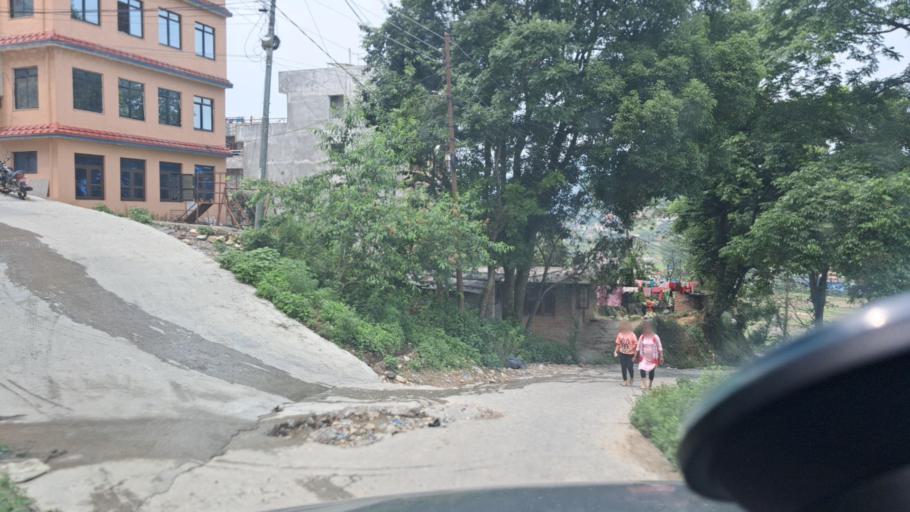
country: NP
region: Central Region
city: Banepa
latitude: 27.6190
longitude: 85.5481
